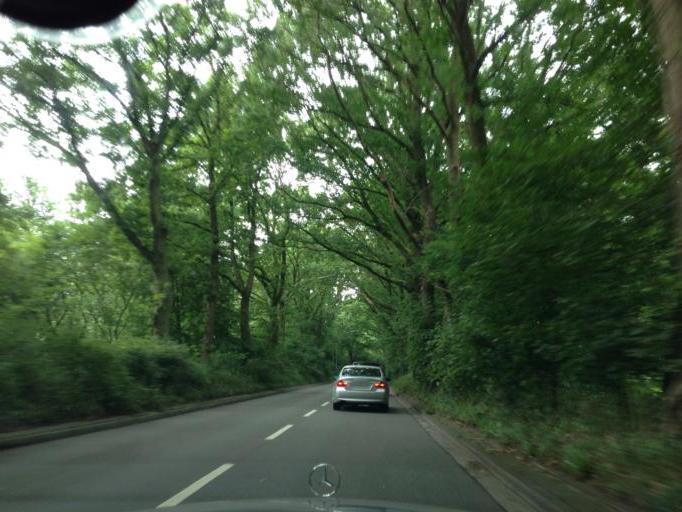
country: DE
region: Hamburg
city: Sasel
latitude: 53.6390
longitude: 10.1297
